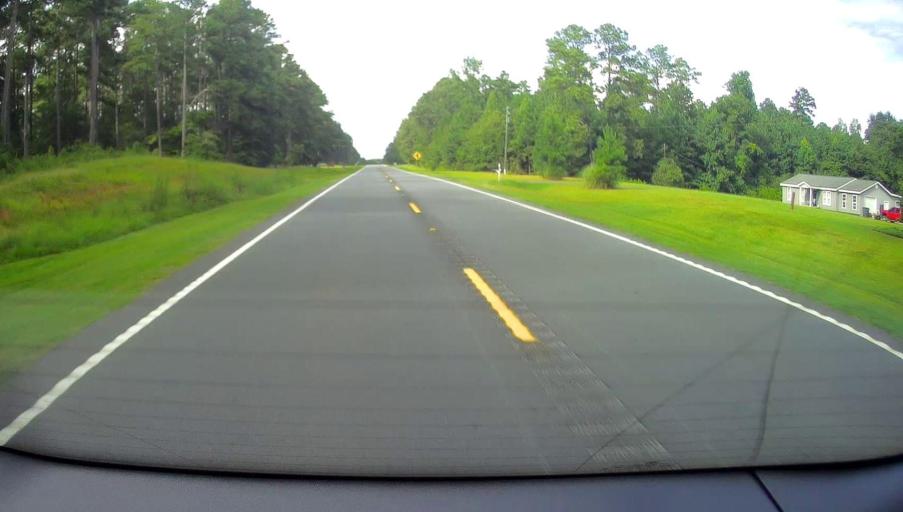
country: US
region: Georgia
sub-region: Meriwether County
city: Manchester
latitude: 32.9692
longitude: -84.6008
